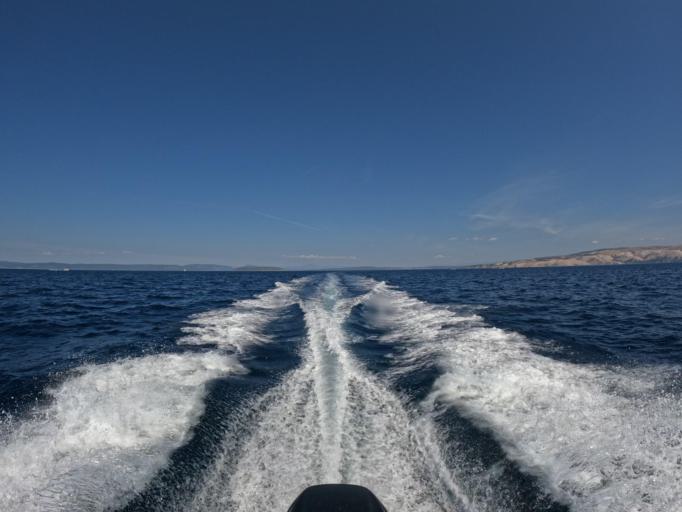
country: HR
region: Primorsko-Goranska
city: Punat
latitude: 44.9019
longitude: 14.6320
